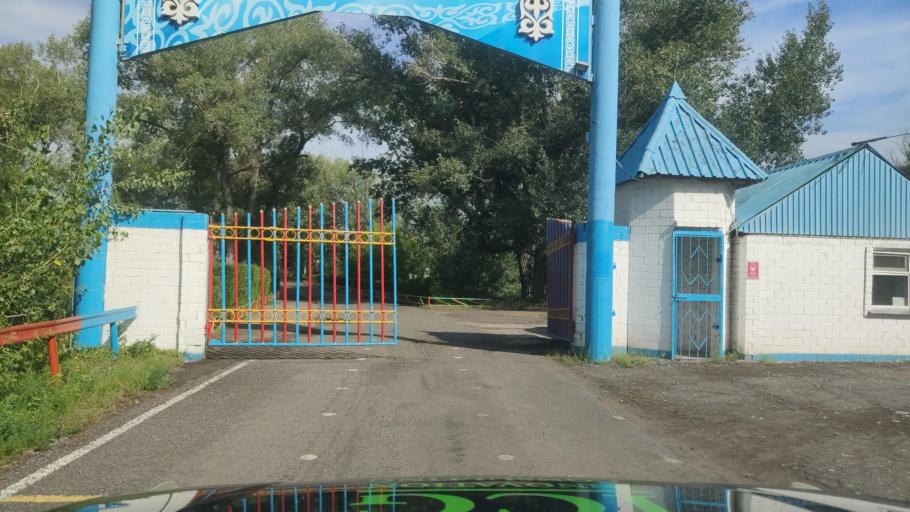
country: KZ
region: Pavlodar
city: Leninskiy
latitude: 52.4769
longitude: 76.8010
